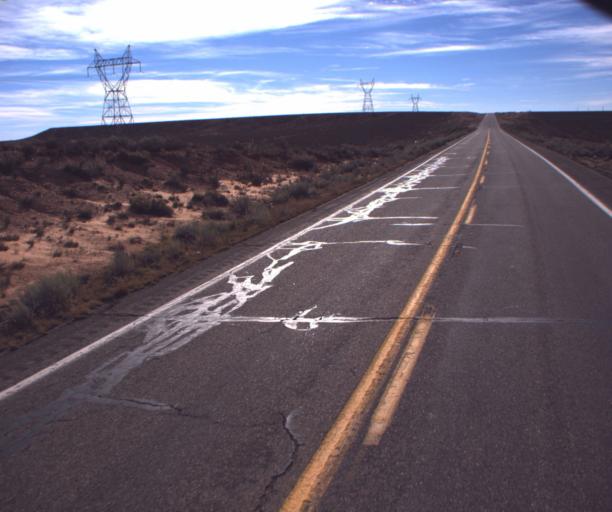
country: US
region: Arizona
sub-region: Coconino County
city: LeChee
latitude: 36.8050
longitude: -111.3056
